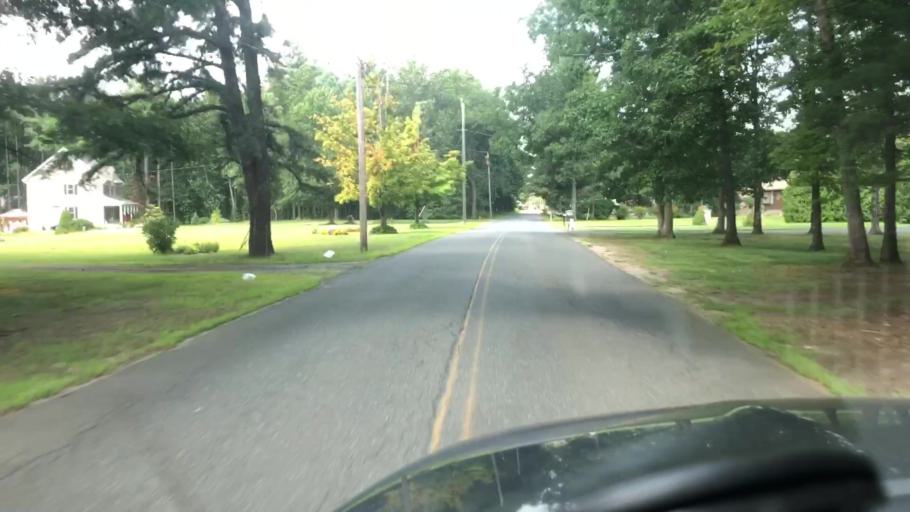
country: US
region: Massachusetts
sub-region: Hampshire County
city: Southampton
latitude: 42.1966
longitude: -72.6917
